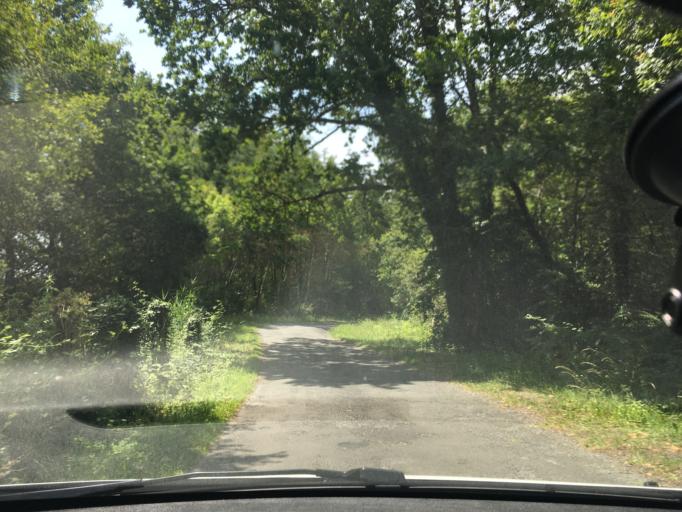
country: FR
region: Aquitaine
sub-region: Departement de la Gironde
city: Lesparre-Medoc
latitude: 45.2800
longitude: -0.9101
